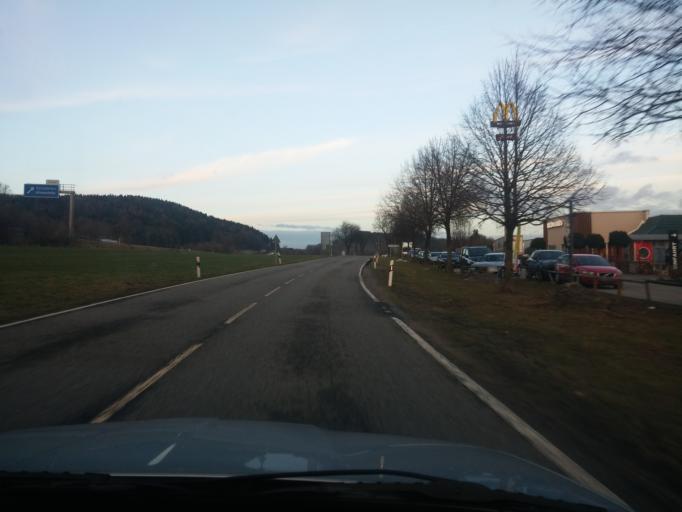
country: DE
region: Baden-Wuerttemberg
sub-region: Tuebingen Region
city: Aichstetten
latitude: 47.8792
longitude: 10.0374
